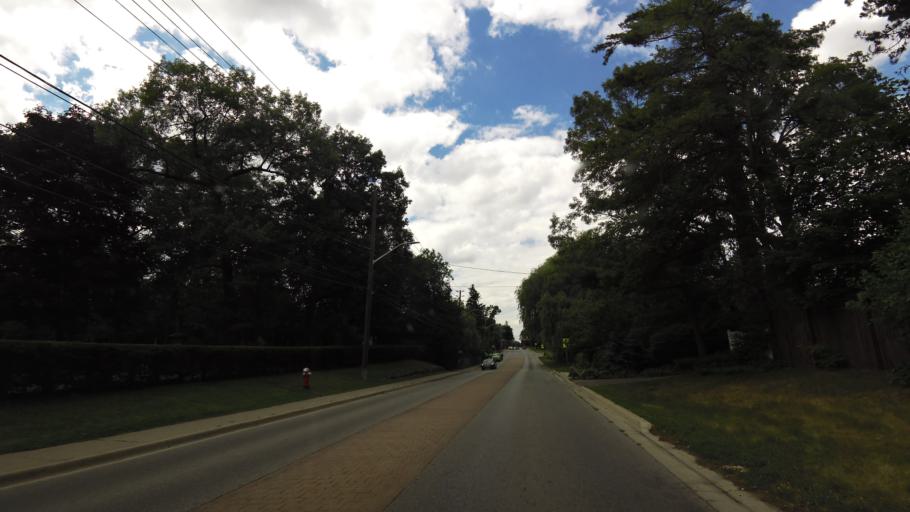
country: CA
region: Ontario
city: Mississauga
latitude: 43.5243
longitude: -79.6335
